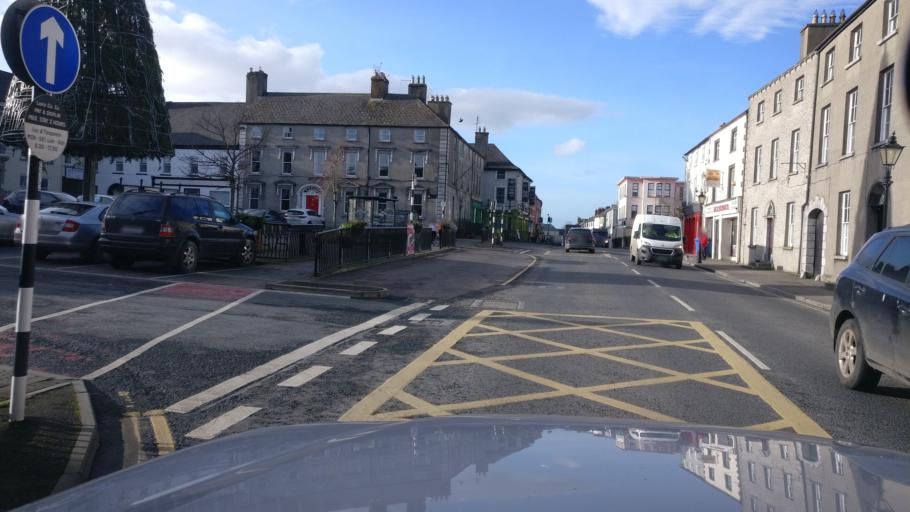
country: IE
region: Leinster
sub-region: Laois
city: Mountmellick
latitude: 53.1173
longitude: -7.3266
